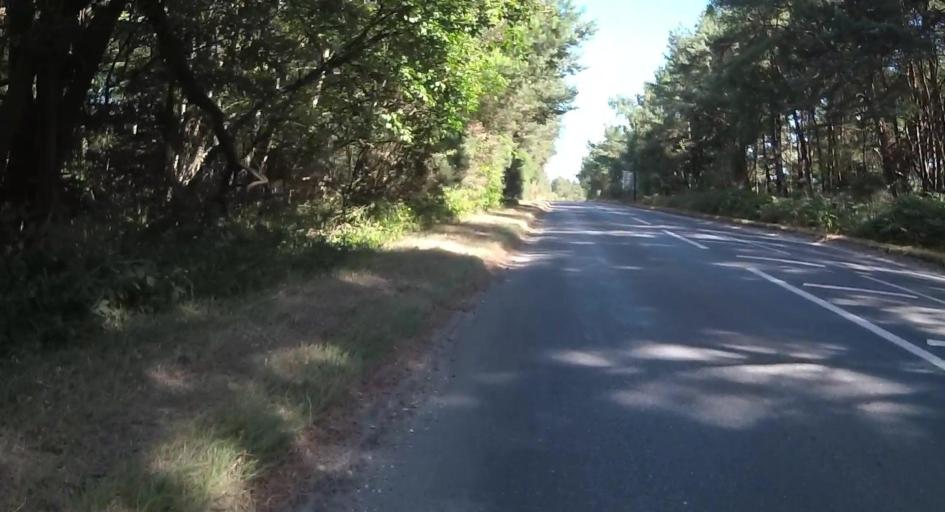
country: GB
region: England
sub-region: Dorset
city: Wool
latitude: 50.7075
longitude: -2.2055
